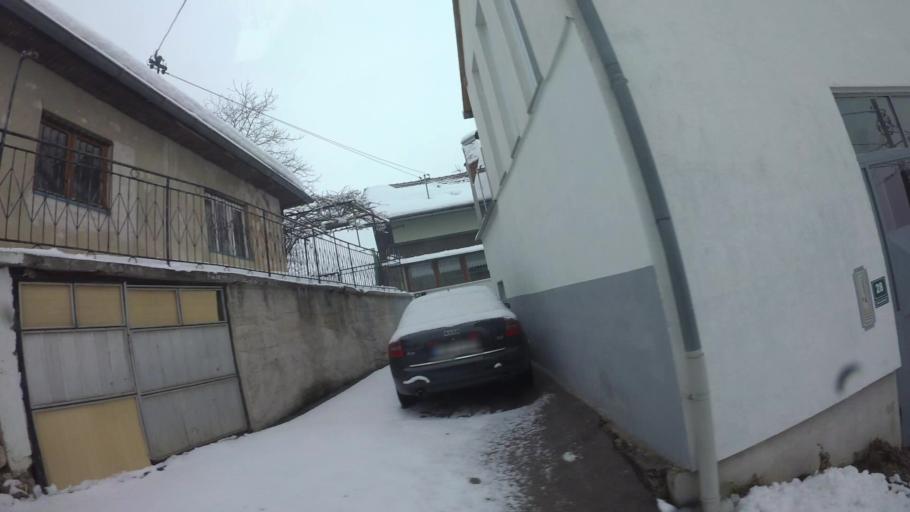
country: BA
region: Federation of Bosnia and Herzegovina
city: Kobilja Glava
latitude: 43.8471
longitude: 18.4226
